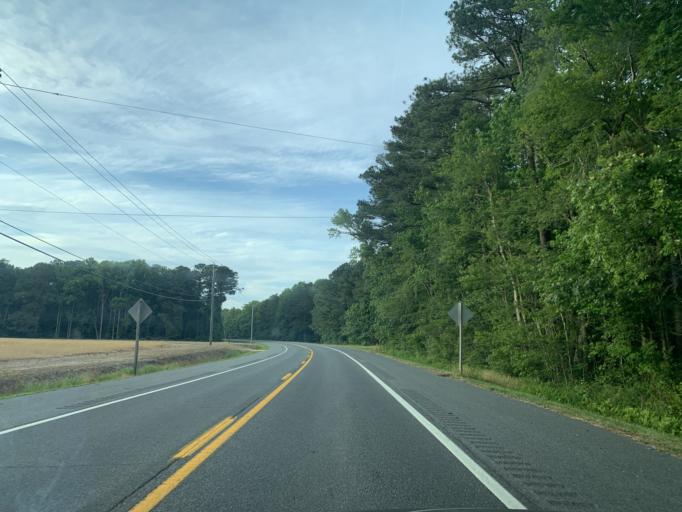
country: US
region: Virginia
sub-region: Accomack County
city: Captains Cove
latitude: 38.0644
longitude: -75.4013
